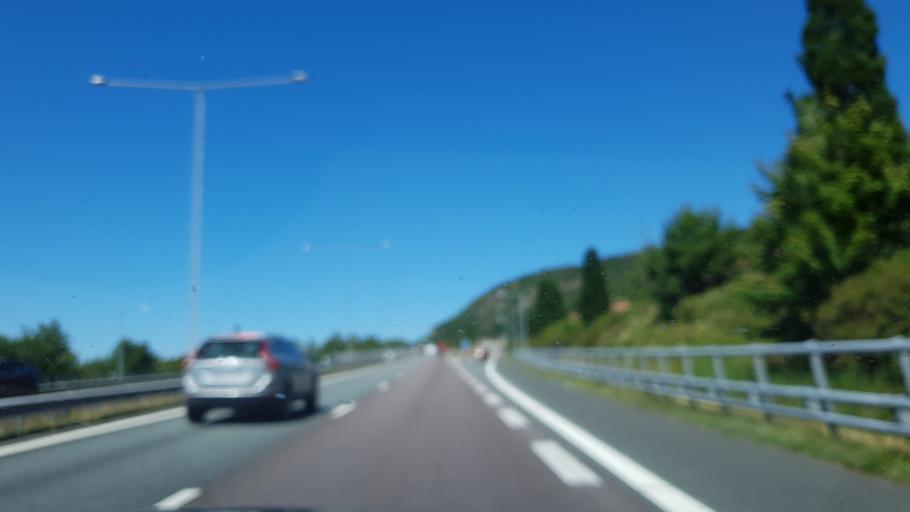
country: SE
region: Joenkoeping
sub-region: Jonkopings Kommun
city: Huskvarna
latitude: 57.8114
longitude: 14.2717
